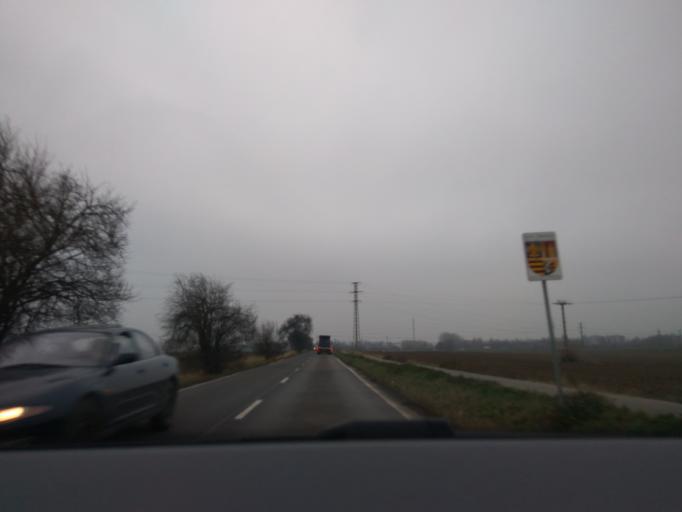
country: CZ
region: Central Bohemia
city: Hovorcovice
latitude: 50.1743
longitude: 14.5192
